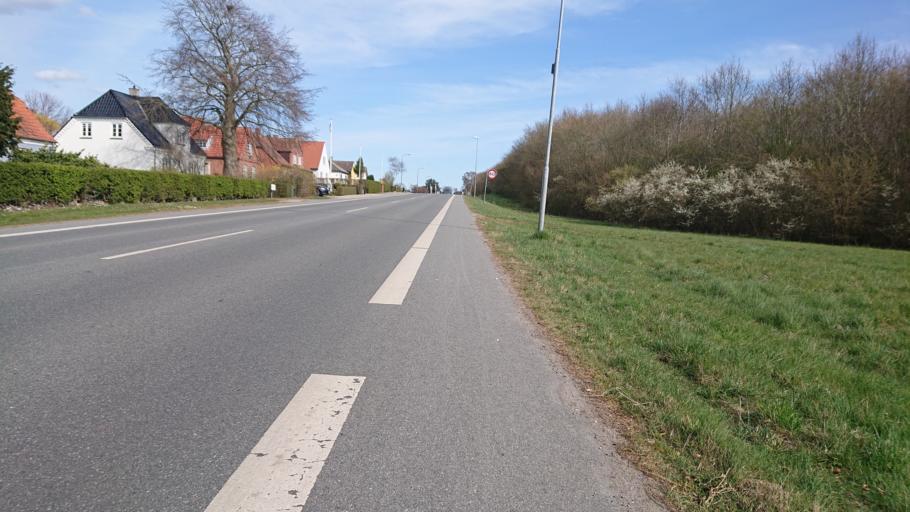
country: DK
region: South Denmark
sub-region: Nyborg Kommune
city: Nyborg
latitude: 55.3096
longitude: 10.7565
